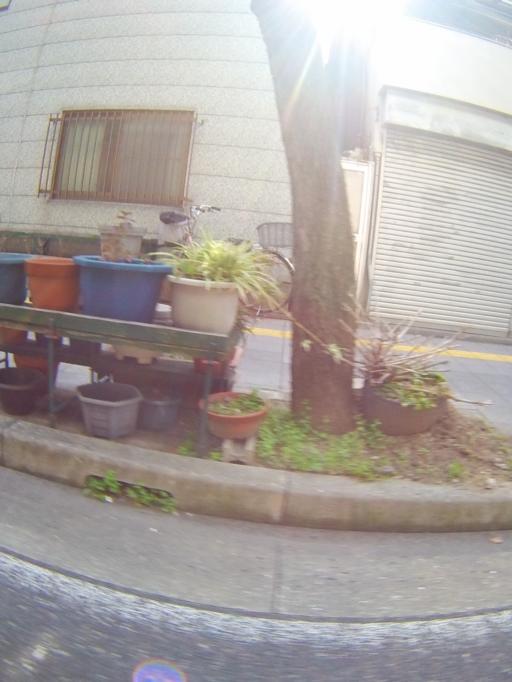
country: JP
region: Osaka
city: Osaka-shi
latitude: 34.6741
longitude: 135.4590
